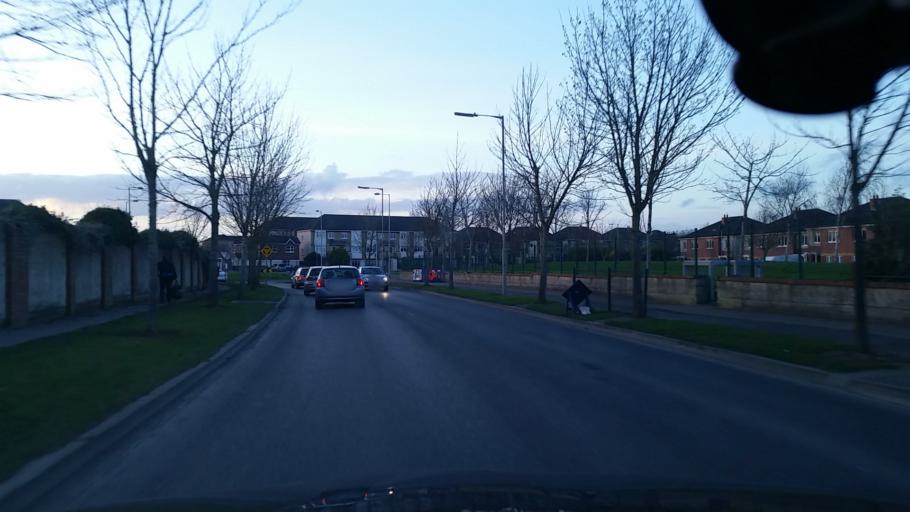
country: IE
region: Leinster
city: Hartstown
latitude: 53.4017
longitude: -6.4353
